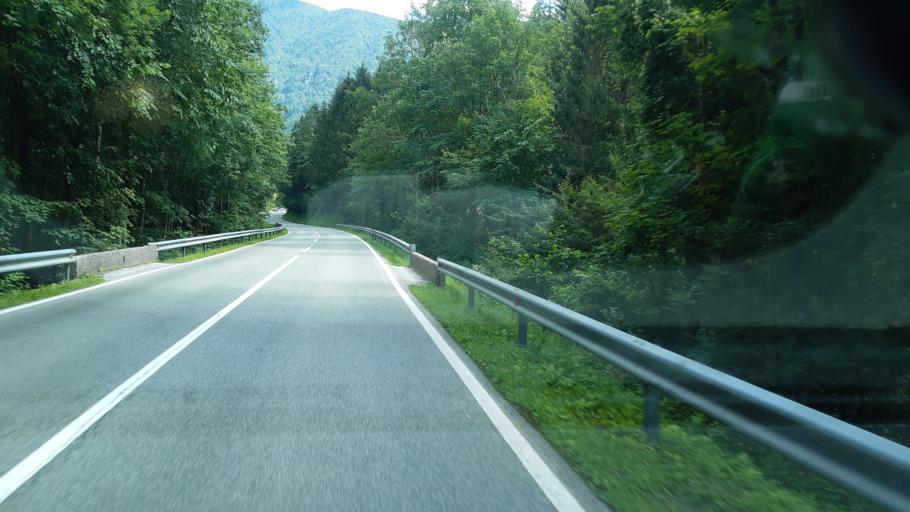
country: SI
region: Trzic
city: Trzic
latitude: 46.3757
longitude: 14.2987
